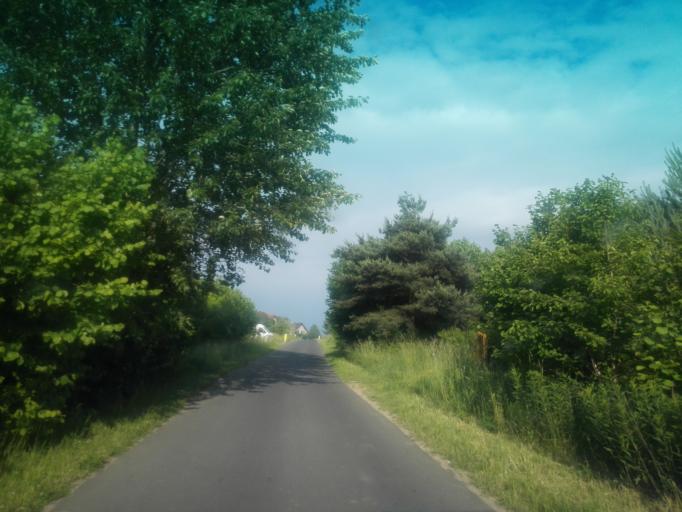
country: PL
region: Silesian Voivodeship
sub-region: Powiat czestochowski
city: Mstow
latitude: 50.8318
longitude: 19.3036
